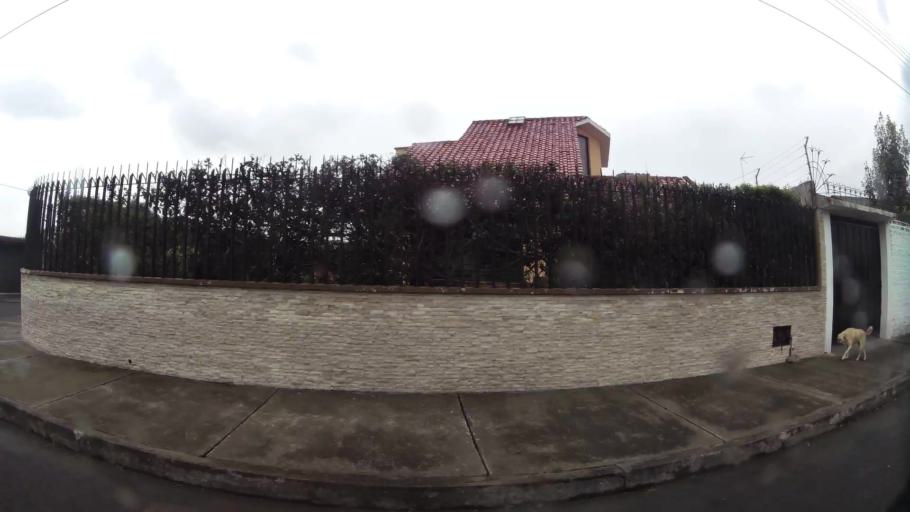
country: EC
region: Pichincha
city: Sangolqui
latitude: -0.2875
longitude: -78.4633
